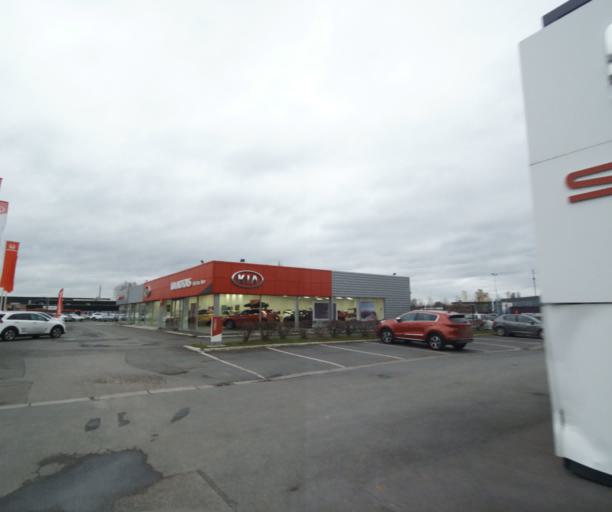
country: FR
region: Nord-Pas-de-Calais
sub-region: Departement du Nord
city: Bruay-sur-l'Escaut
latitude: 50.3872
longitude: 3.5521
